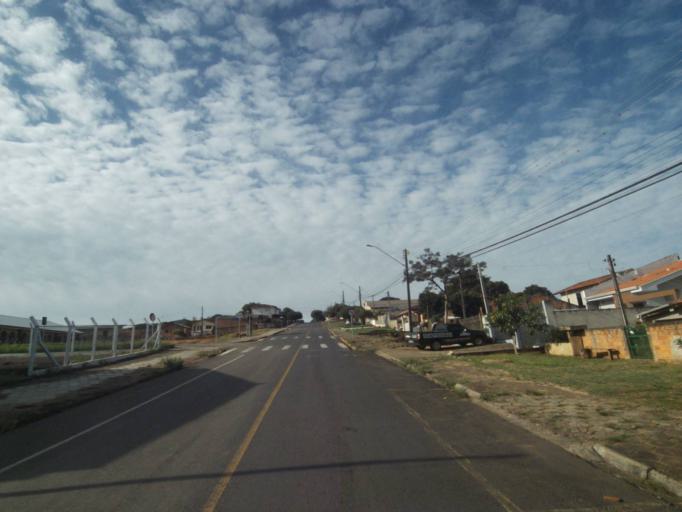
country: BR
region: Parana
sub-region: Telemaco Borba
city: Telemaco Borba
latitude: -24.3444
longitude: -50.6121
